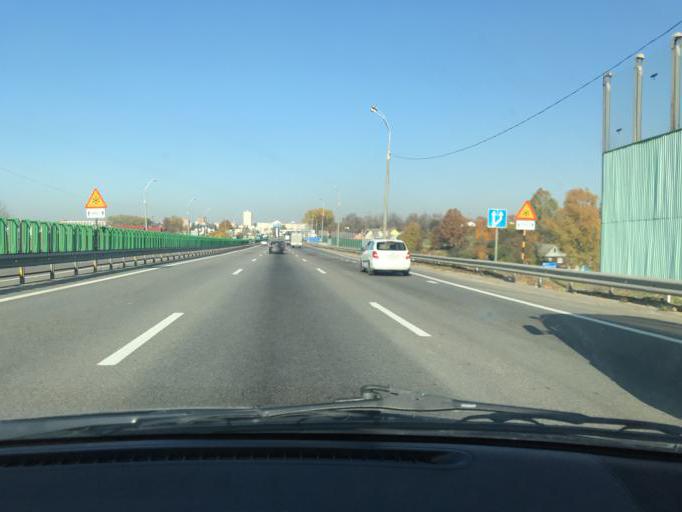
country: BY
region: Minsk
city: Syenitsa
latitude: 53.8286
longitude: 27.5340
